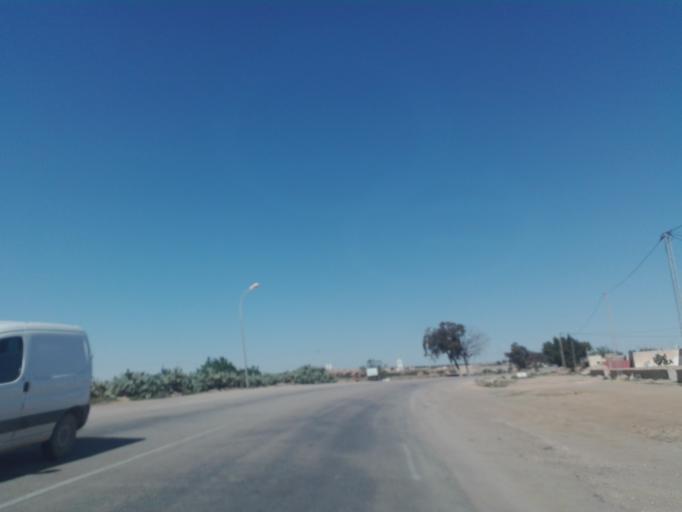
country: TN
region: Safaqis
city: Bi'r `Ali Bin Khalifah
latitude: 34.7414
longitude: 10.3704
